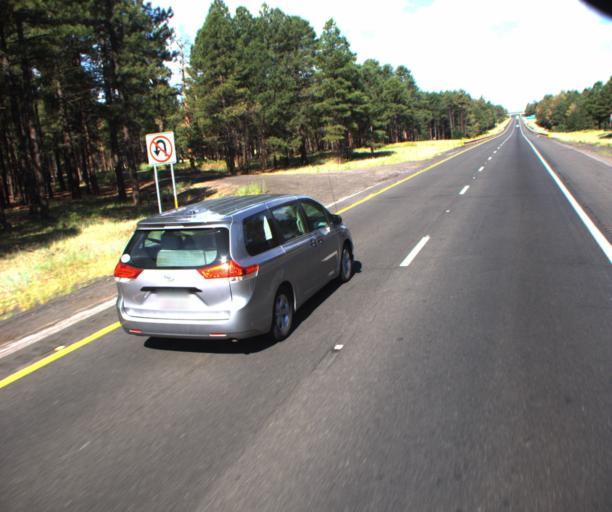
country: US
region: Arizona
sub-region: Coconino County
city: Flagstaff
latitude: 35.1796
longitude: -111.6826
